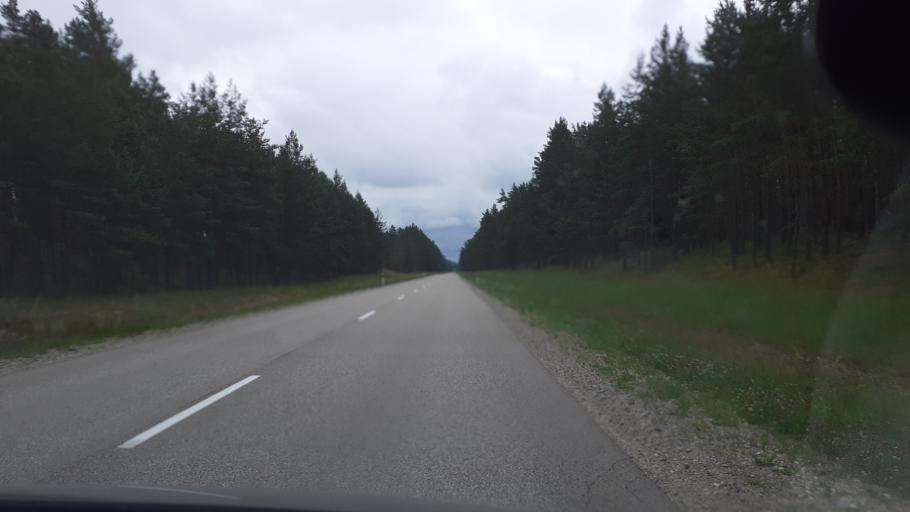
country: LV
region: Ventspils Rajons
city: Piltene
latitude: 57.1157
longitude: 21.7532
